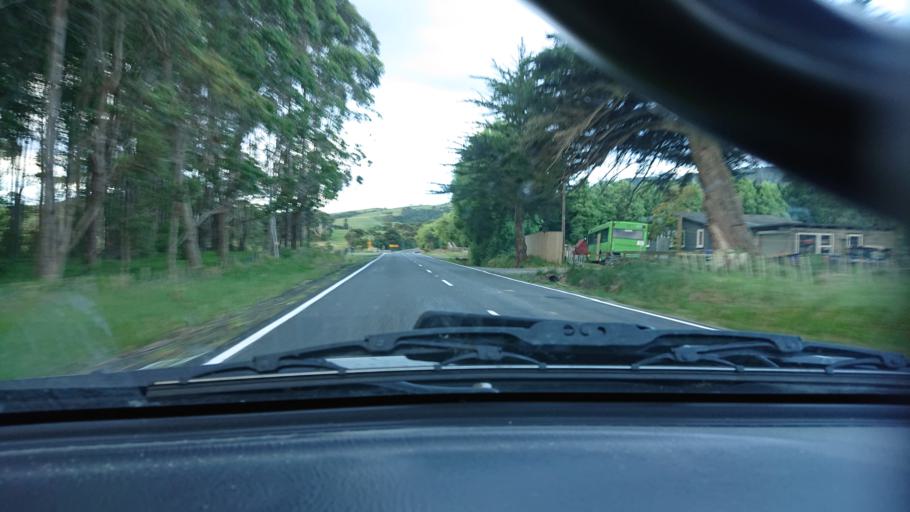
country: NZ
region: Auckland
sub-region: Auckland
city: Parakai
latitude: -36.4639
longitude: 174.4457
